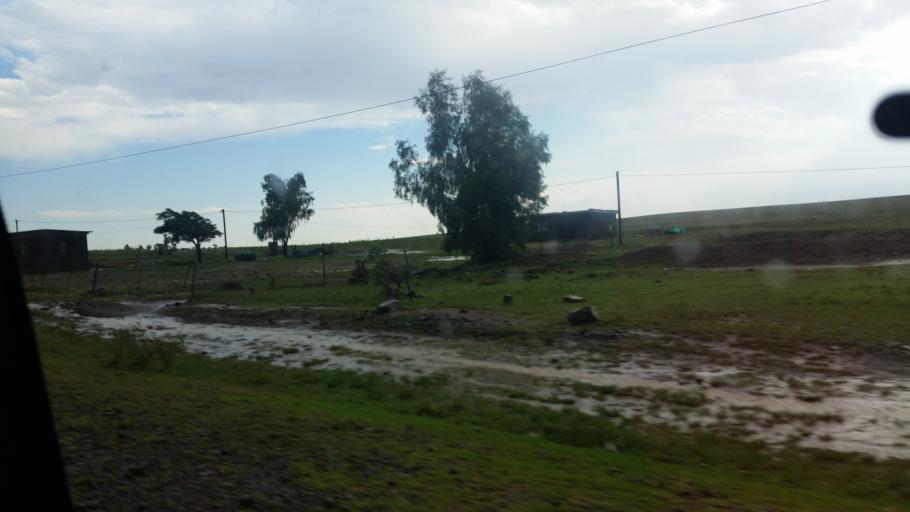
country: LS
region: Mafeteng
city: Mafeteng
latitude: -29.7607
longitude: 27.1737
